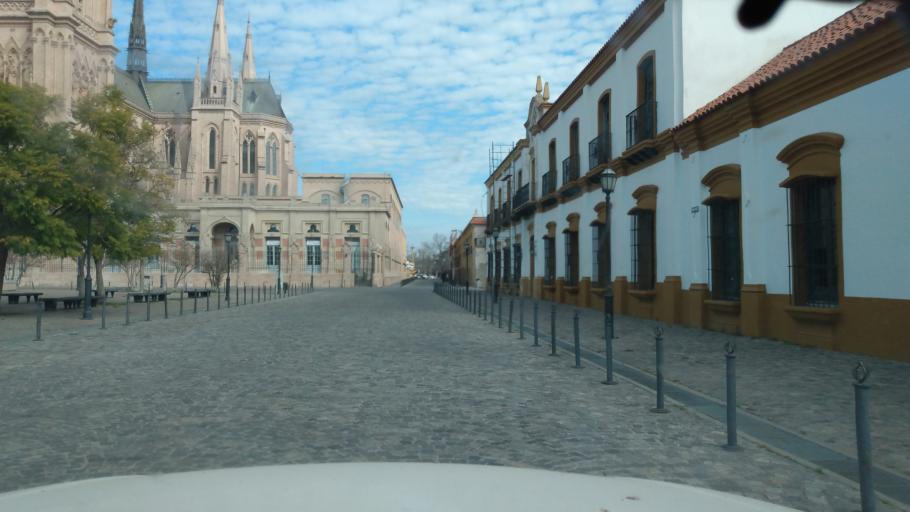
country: AR
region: Buenos Aires
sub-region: Partido de Lujan
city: Lujan
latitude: -34.5632
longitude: -59.1216
